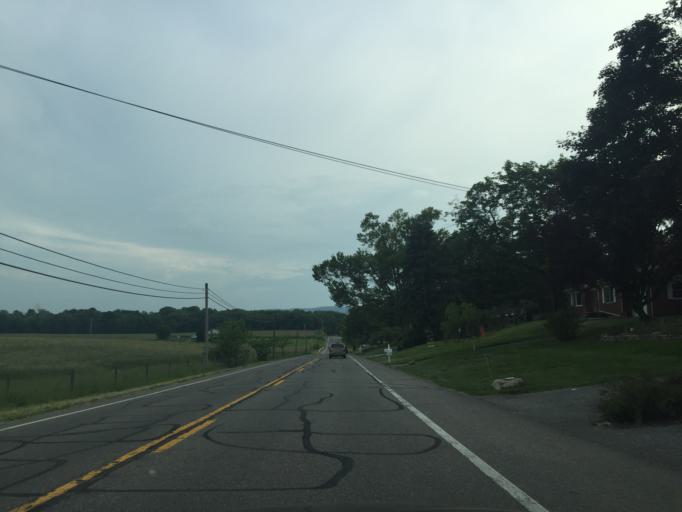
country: US
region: Maryland
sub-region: Frederick County
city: Brunswick
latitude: 39.3338
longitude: -77.6448
